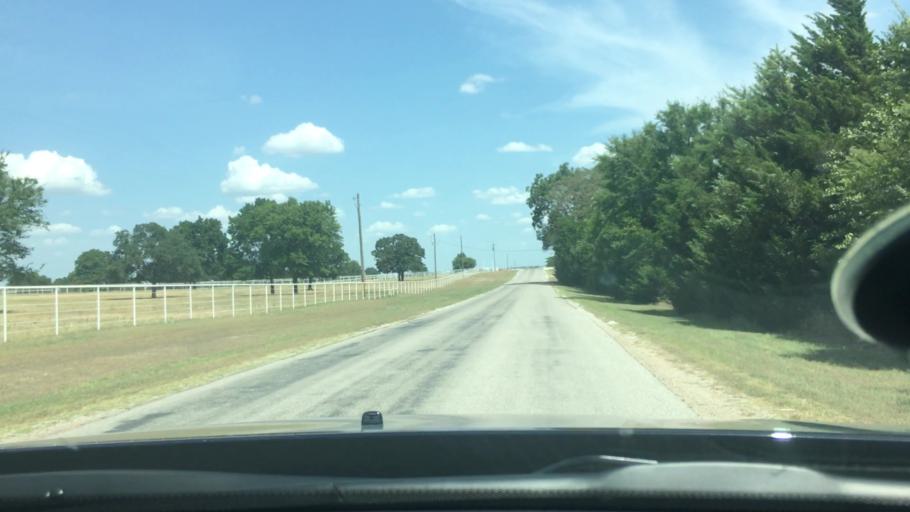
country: US
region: Oklahoma
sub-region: Love County
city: Marietta
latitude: 34.0433
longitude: -97.1957
